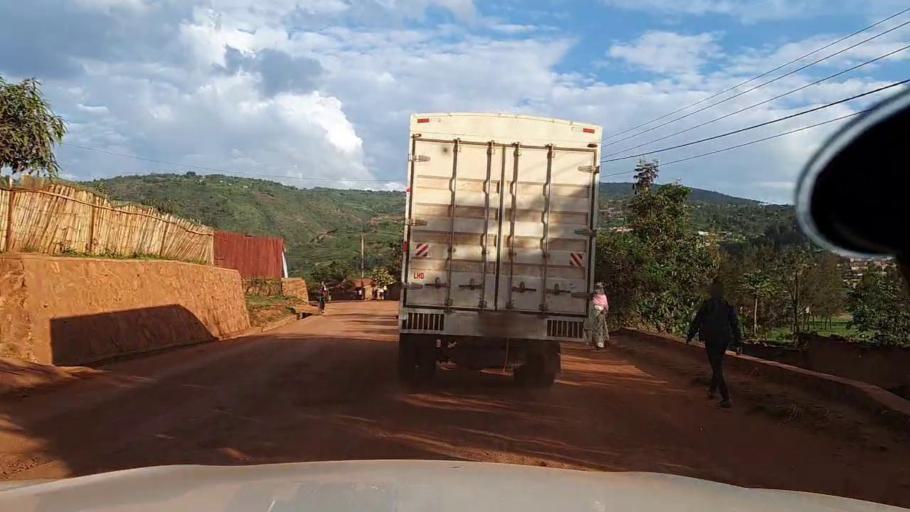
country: RW
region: Kigali
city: Kigali
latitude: -1.9474
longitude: 30.0171
